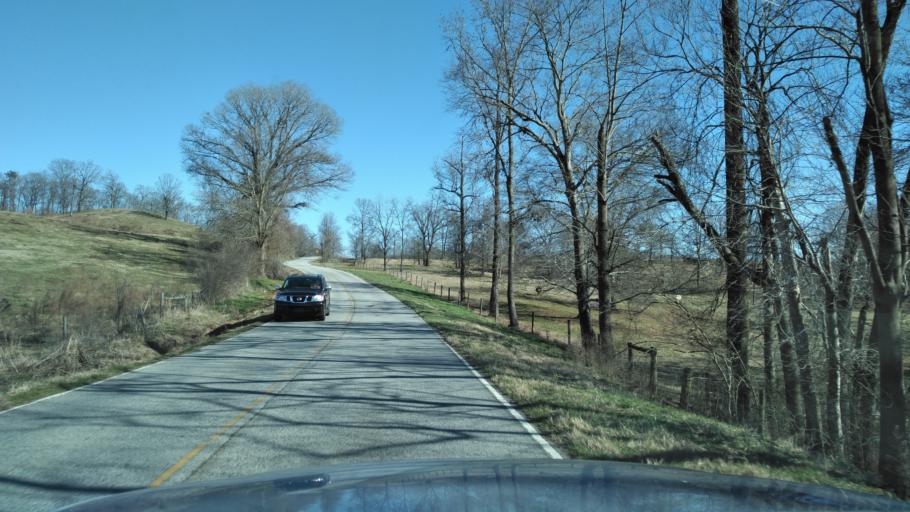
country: US
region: Georgia
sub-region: Hall County
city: Lula
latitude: 34.3188
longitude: -83.7019
